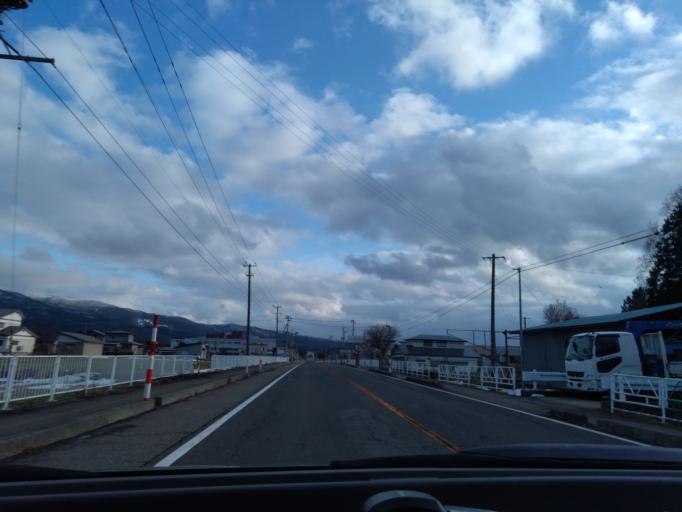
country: JP
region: Akita
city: Omagari
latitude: 39.4056
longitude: 140.5588
